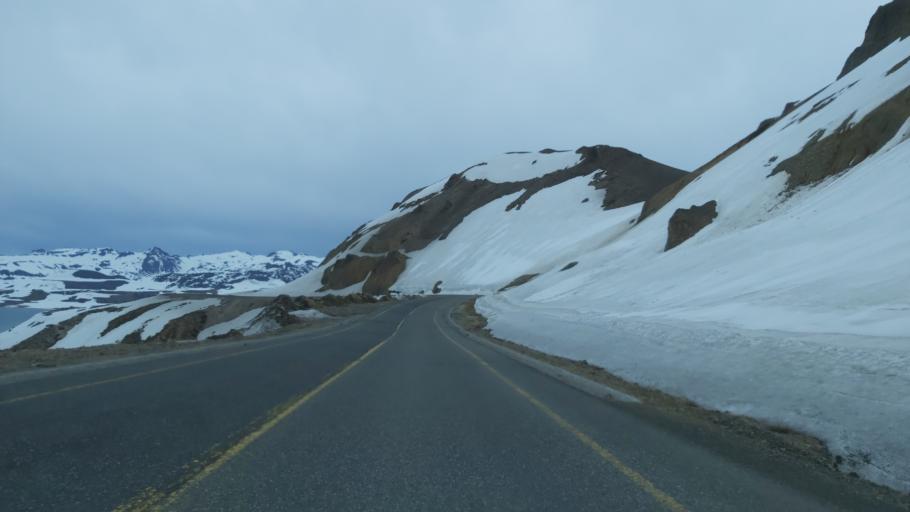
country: CL
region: Maule
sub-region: Provincia de Linares
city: Colbun
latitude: -36.0139
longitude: -70.5127
